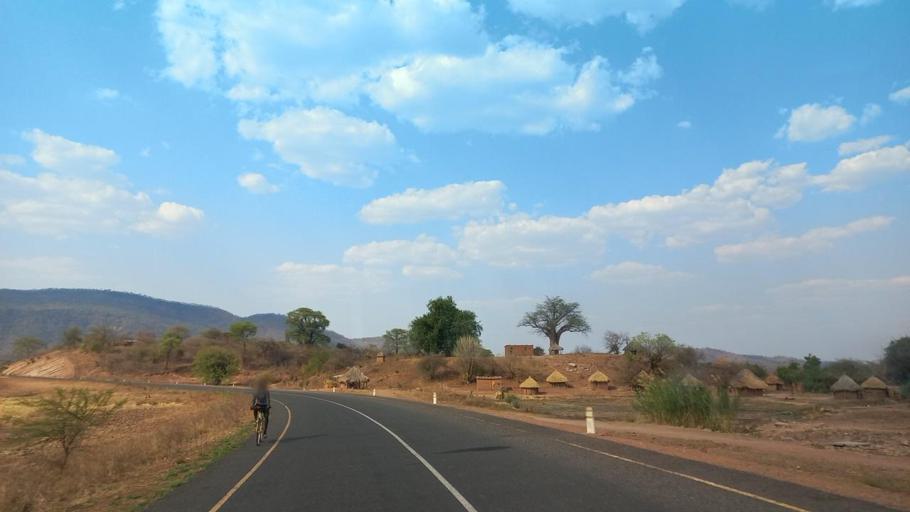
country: ZM
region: Lusaka
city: Luangwa
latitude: -15.0629
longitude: 30.2099
